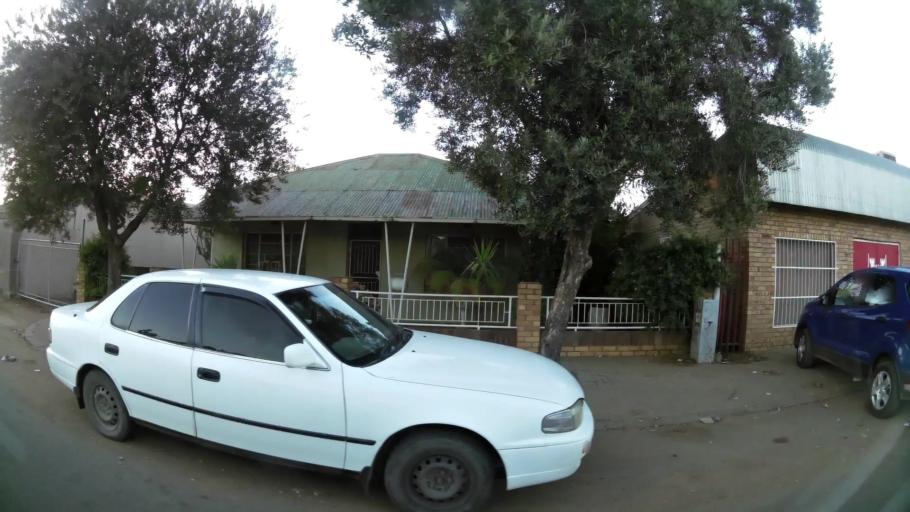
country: ZA
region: Northern Cape
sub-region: Frances Baard District Municipality
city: Kimberley
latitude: -28.7302
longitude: 24.7744
